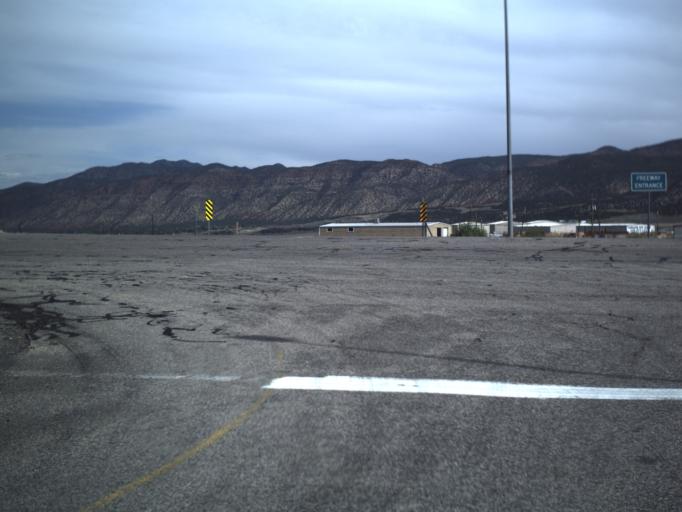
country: US
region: Utah
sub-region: Iron County
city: Parowan
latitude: 37.8573
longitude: -112.8282
